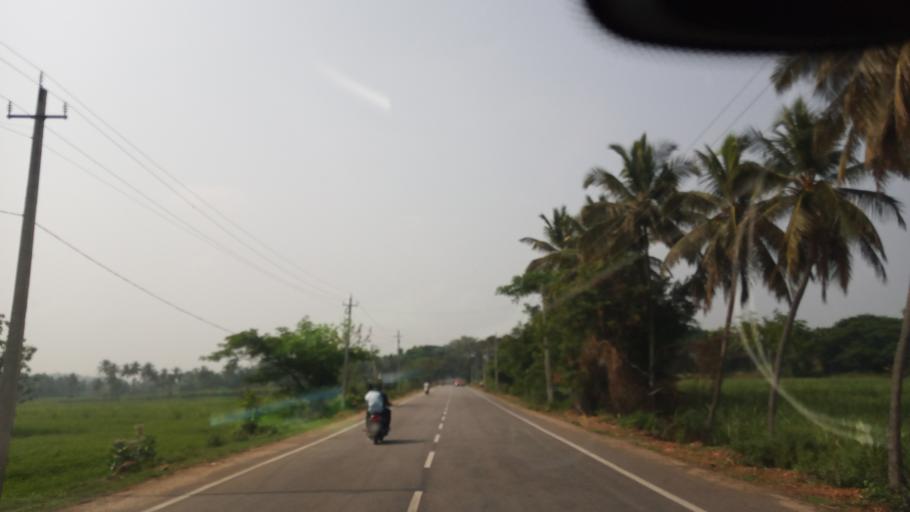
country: IN
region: Karnataka
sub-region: Mandya
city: Pandavapura
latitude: 12.5187
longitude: 76.6736
